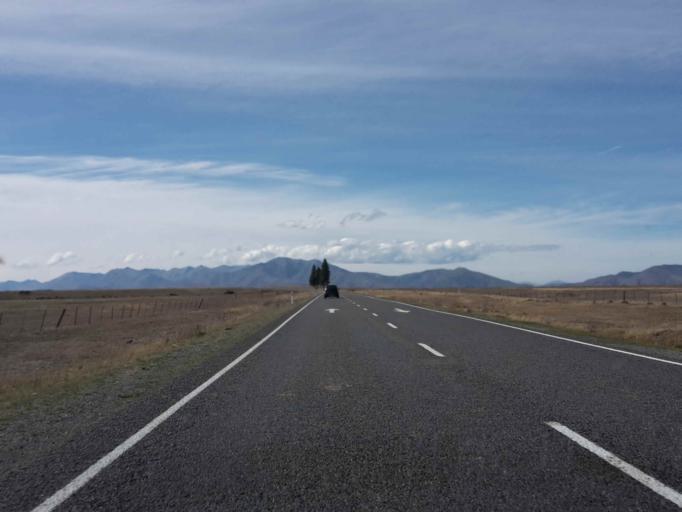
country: NZ
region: Canterbury
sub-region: Timaru District
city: Pleasant Point
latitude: -44.1724
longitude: 170.3276
